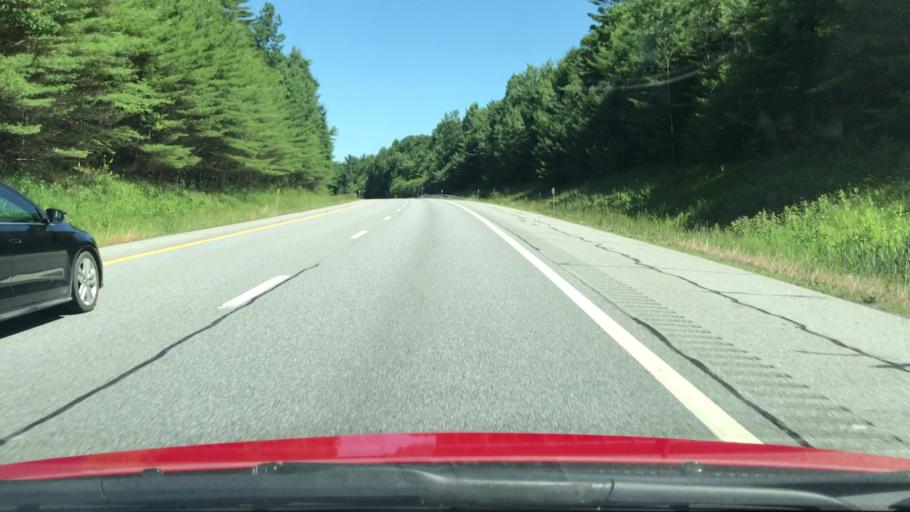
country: US
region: New York
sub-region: Warren County
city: Warrensburg
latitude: 43.5222
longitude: -73.7381
